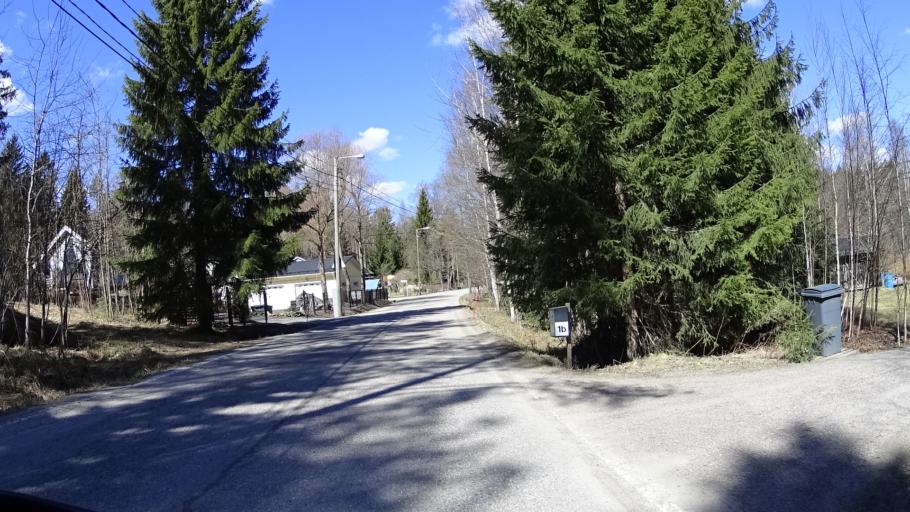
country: FI
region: Uusimaa
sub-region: Helsinki
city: Espoo
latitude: 60.2728
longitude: 24.5158
